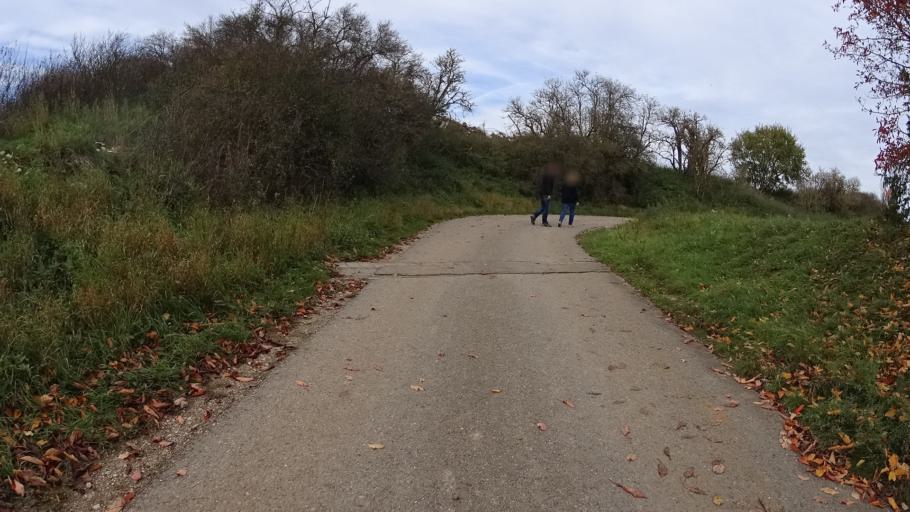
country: DE
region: Bavaria
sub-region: Upper Bavaria
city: Adelschlag
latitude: 48.8650
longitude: 11.2490
